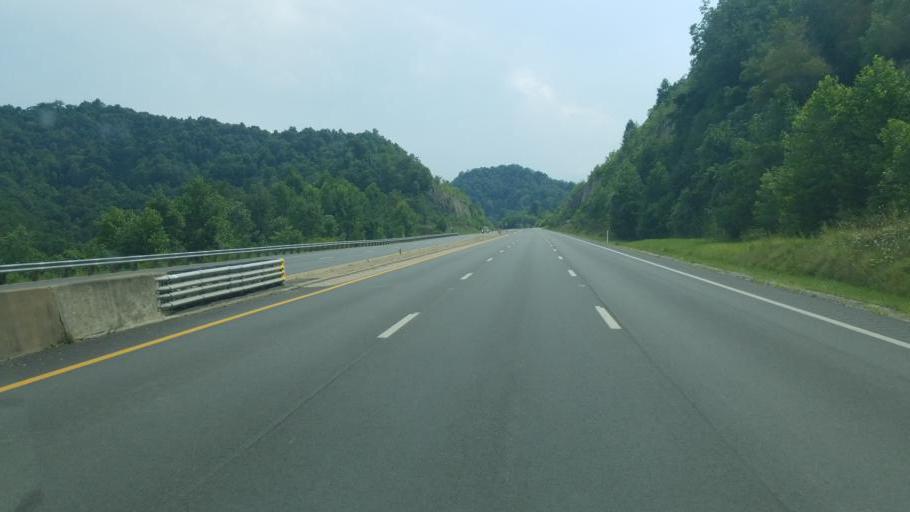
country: US
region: West Virginia
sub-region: Logan County
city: Chapmanville
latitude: 37.9201
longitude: -82.0337
